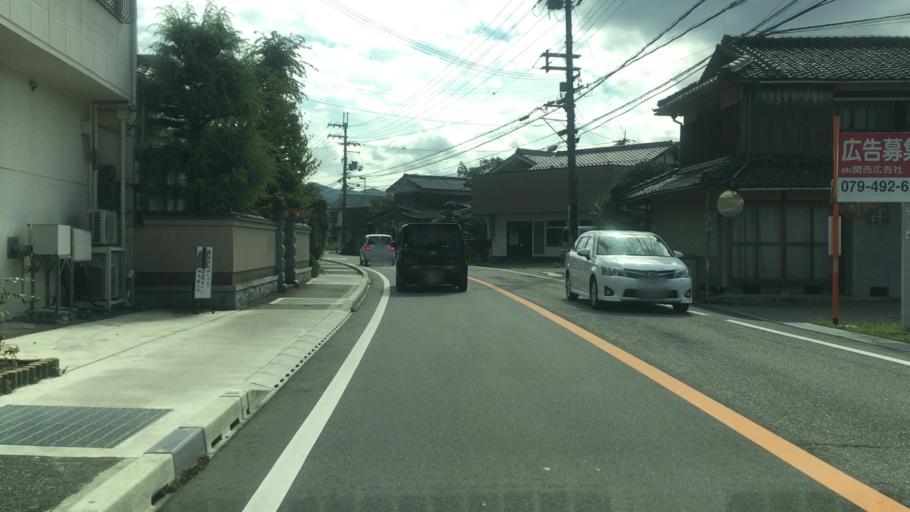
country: JP
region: Kyoto
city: Fukuchiyama
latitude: 35.1517
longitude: 135.0535
